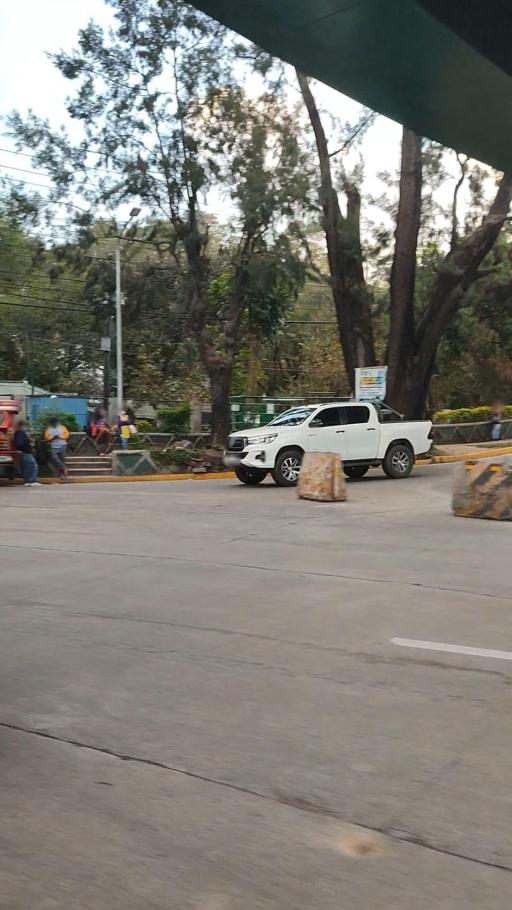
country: PH
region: Cordillera
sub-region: Baguio City
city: Baguio
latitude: 16.4023
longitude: 120.5958
